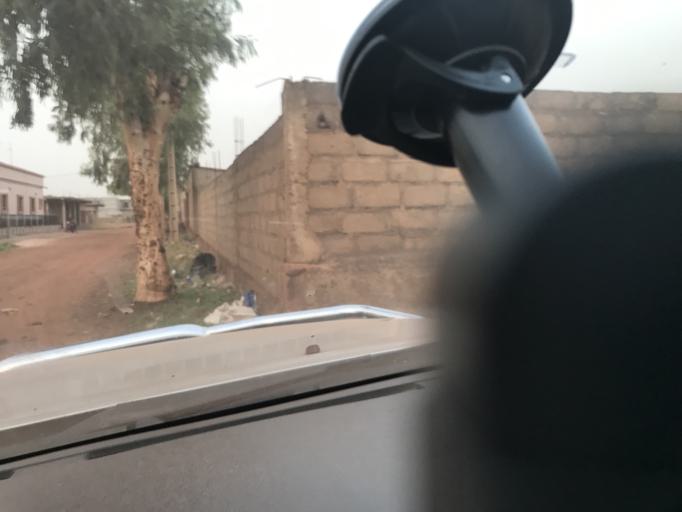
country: ML
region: Bamako
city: Bamako
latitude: 12.6531
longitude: -7.8845
